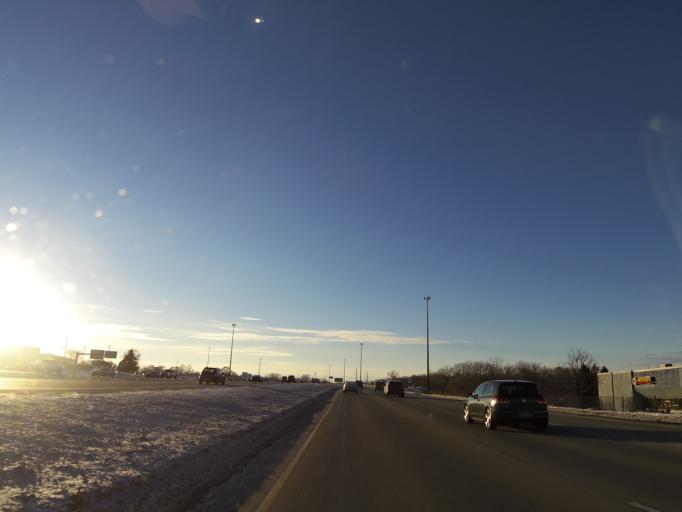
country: US
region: Minnesota
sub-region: Hennepin County
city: Eden Prairie
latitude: 44.8619
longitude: -93.4653
